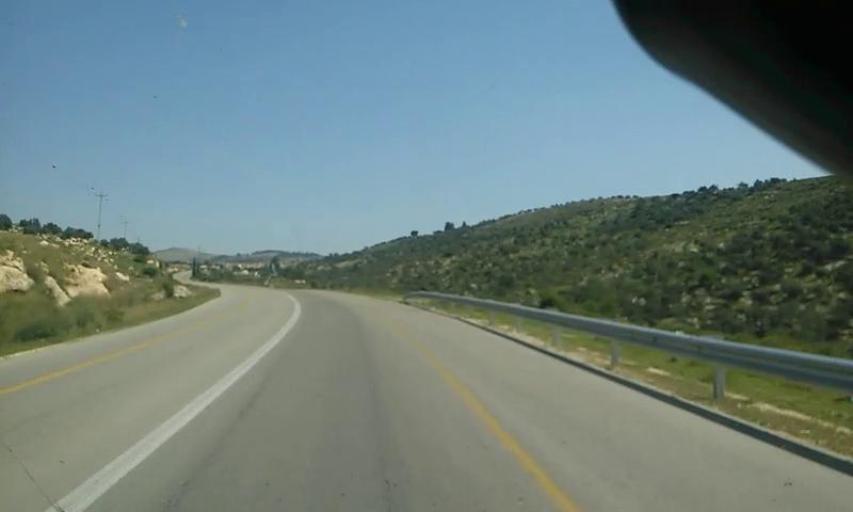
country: PS
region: West Bank
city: Tarqumya
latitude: 31.5639
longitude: 34.9971
